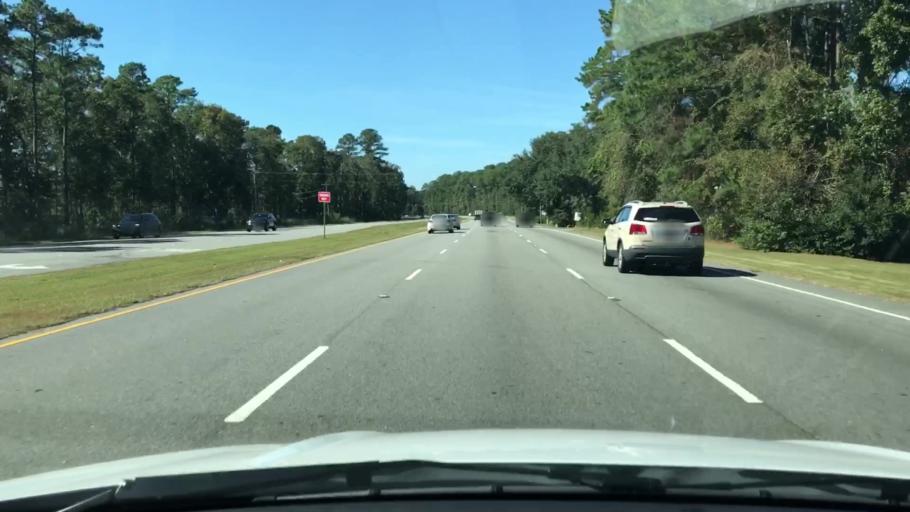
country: US
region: South Carolina
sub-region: Beaufort County
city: Bluffton
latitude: 32.2883
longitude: -80.8946
